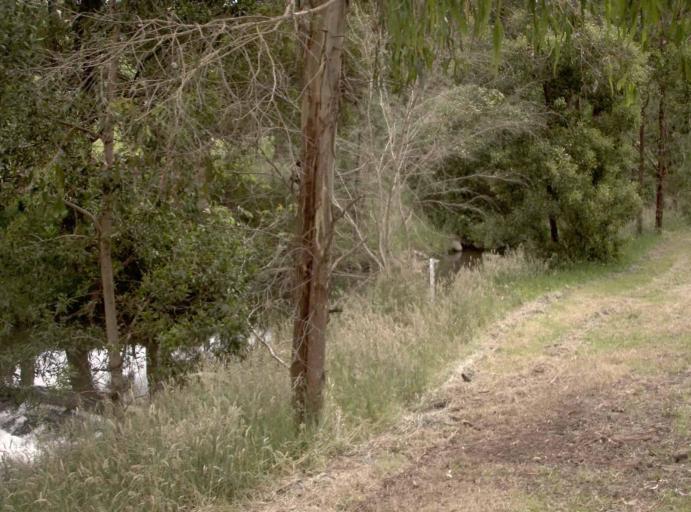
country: AU
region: Victoria
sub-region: Latrobe
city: Traralgon
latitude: -38.4696
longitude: 146.5554
